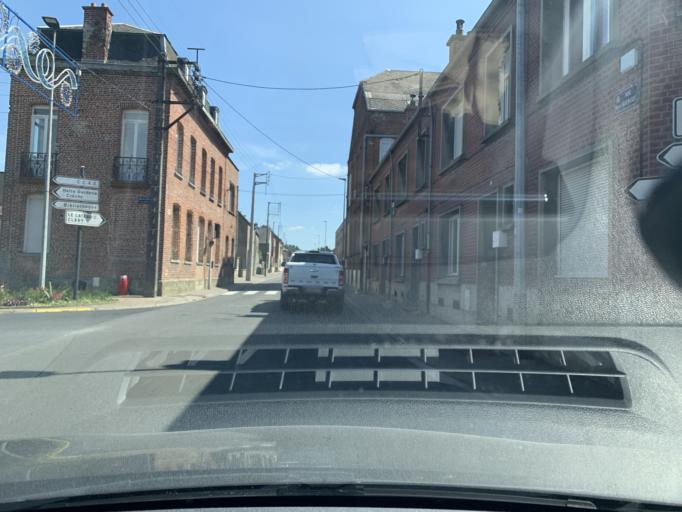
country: FR
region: Nord-Pas-de-Calais
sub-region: Departement du Nord
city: Caudry
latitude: 50.1207
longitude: 3.4028
